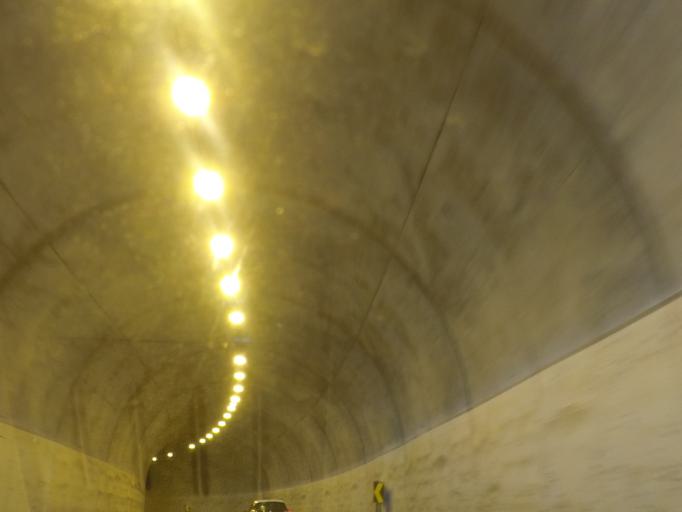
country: PT
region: Madeira
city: Ribeira Brava
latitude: 32.6728
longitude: -17.0621
